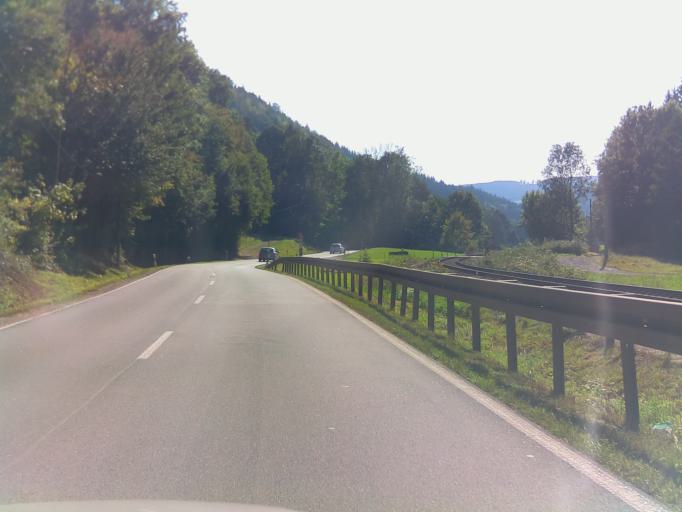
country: DE
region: Thuringia
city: Leutenberg
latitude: 50.5911
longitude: 11.4368
